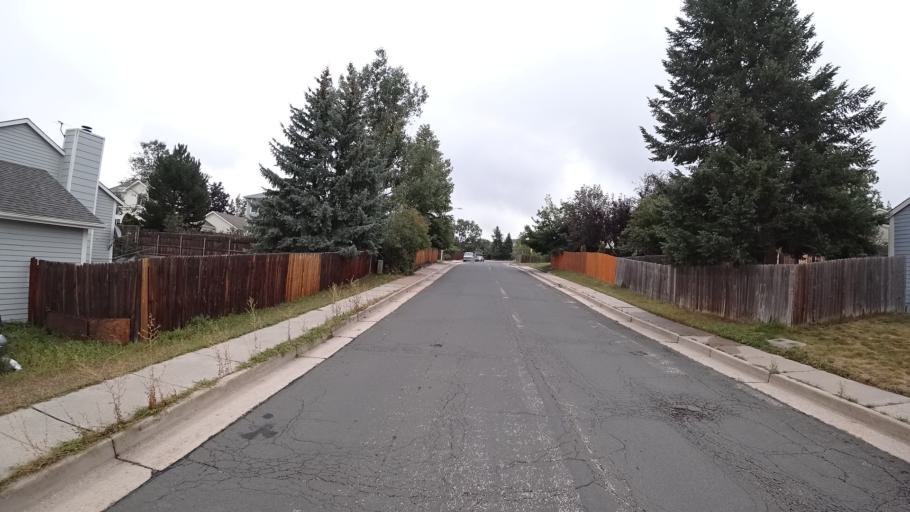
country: US
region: Colorado
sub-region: El Paso County
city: Cimarron Hills
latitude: 38.9272
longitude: -104.7655
